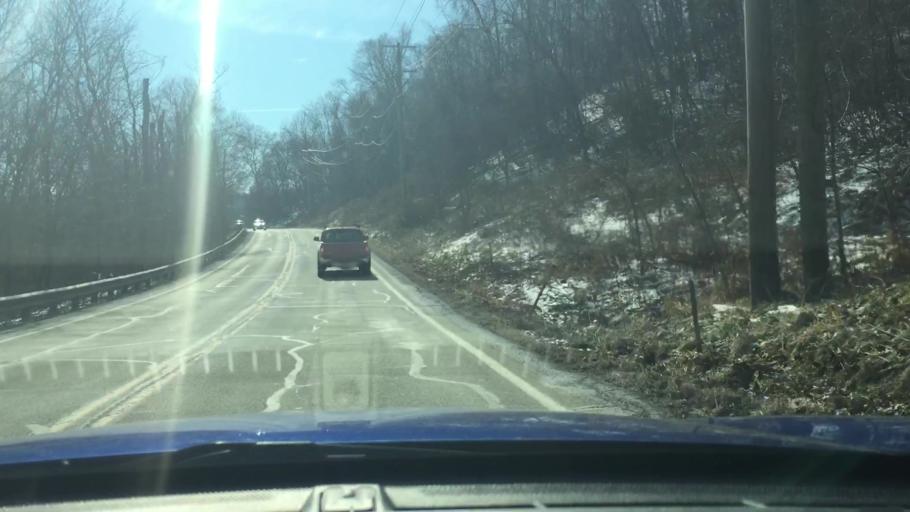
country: US
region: Pennsylvania
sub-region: Washington County
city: Canonsburg
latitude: 40.2851
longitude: -80.1553
